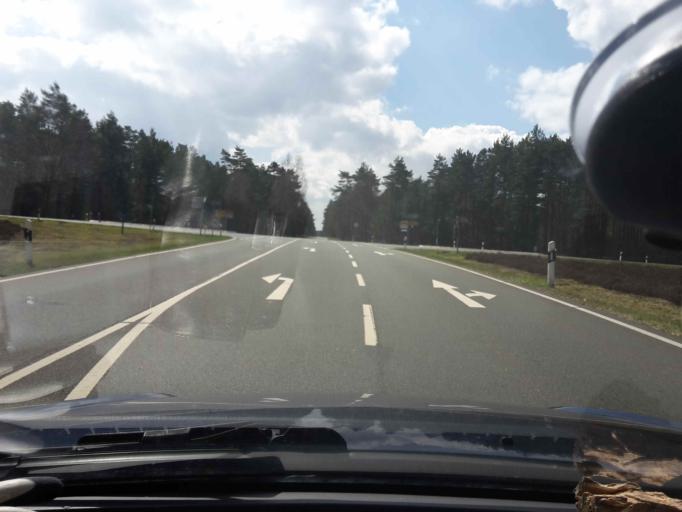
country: DE
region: Lower Saxony
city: Bispingen
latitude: 53.0911
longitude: 10.0456
